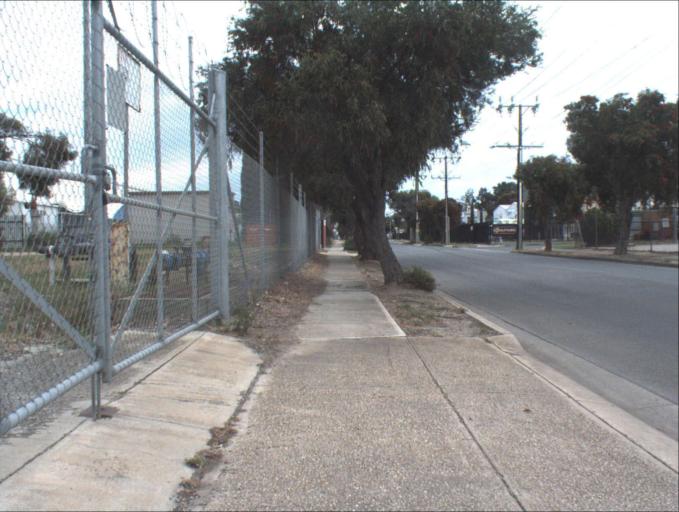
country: AU
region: South Australia
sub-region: Prospect
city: Prospect
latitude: -34.8822
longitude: 138.5789
